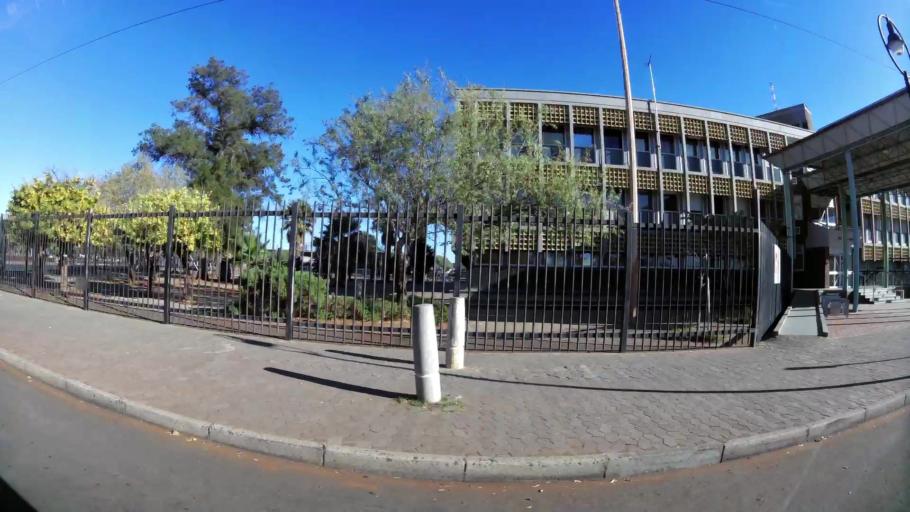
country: ZA
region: Northern Cape
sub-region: Frances Baard District Municipality
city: Kimberley
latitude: -28.7453
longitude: 24.7667
